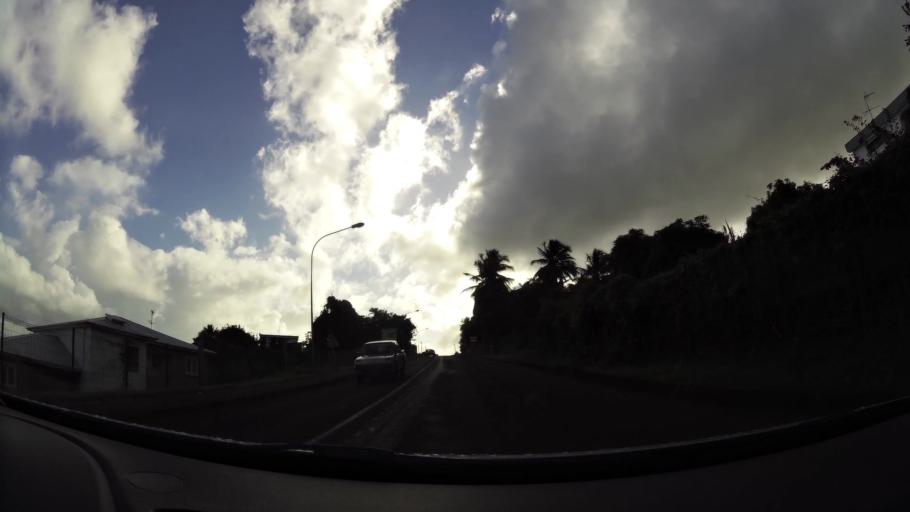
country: MQ
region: Martinique
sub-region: Martinique
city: Ducos
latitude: 14.5775
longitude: -60.9749
